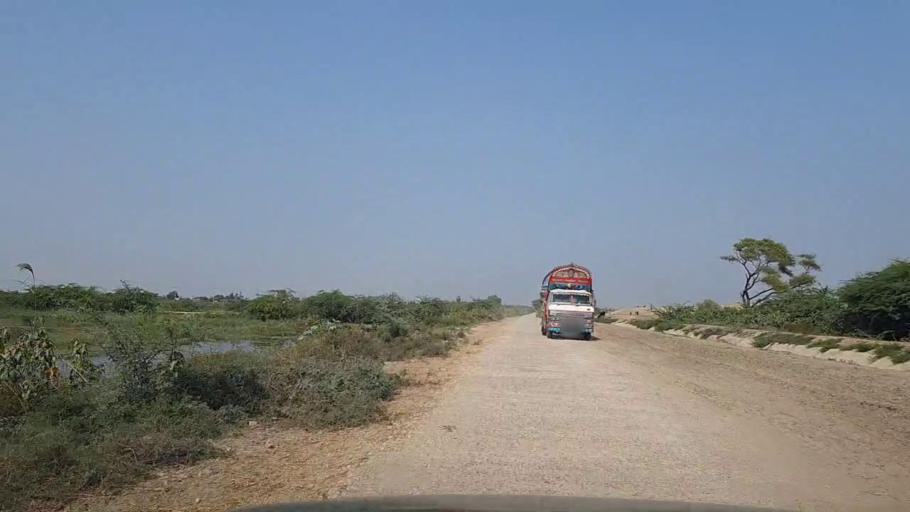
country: PK
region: Sindh
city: Chuhar Jamali
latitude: 24.5231
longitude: 67.9264
